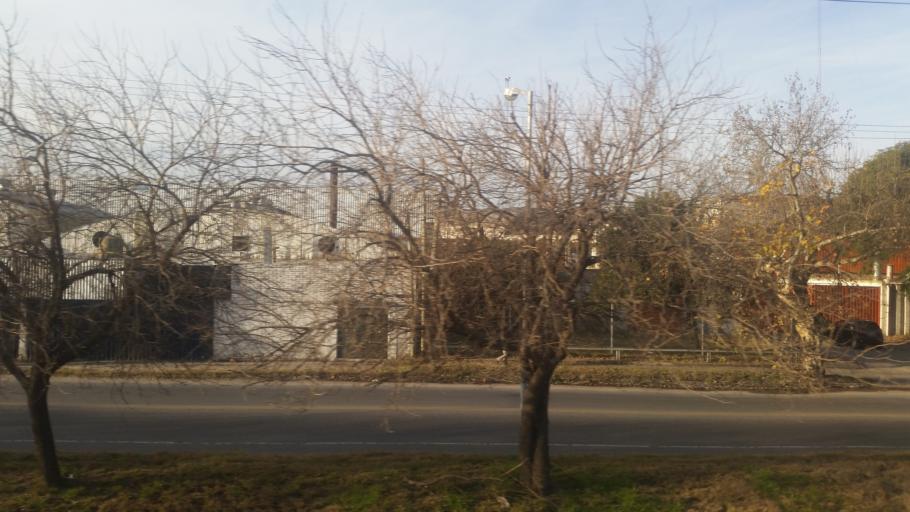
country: AR
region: Cordoba
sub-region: Departamento de Capital
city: Cordoba
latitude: -31.4535
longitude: -64.1151
